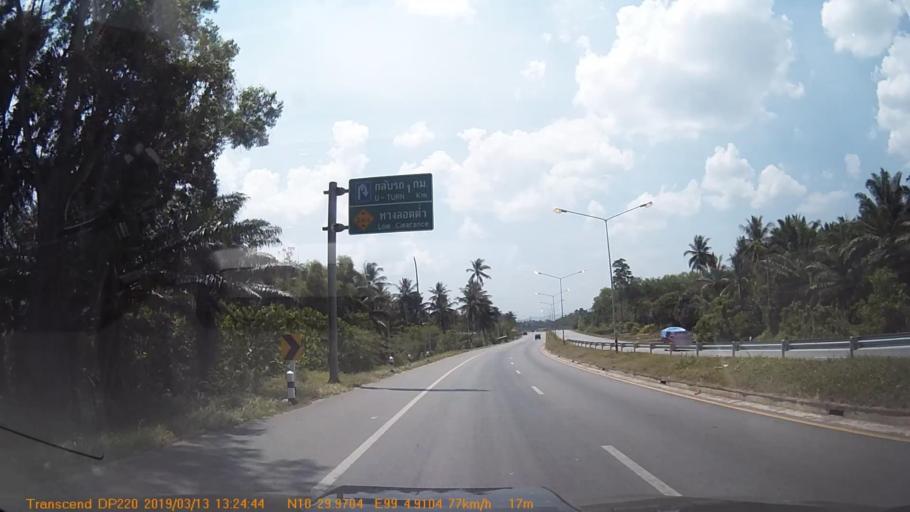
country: TH
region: Chumphon
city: Chumphon
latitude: 10.5016
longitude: 99.0857
